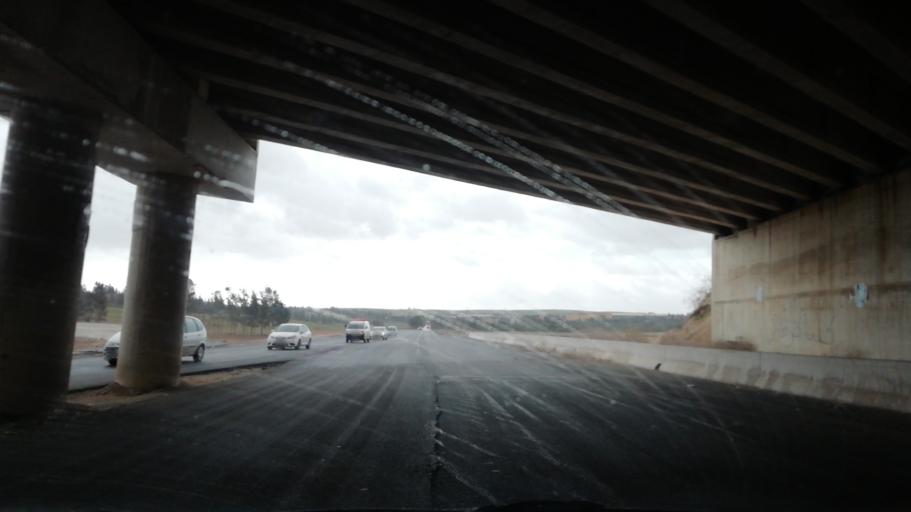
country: DZ
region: Oran
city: Sidi ech Chahmi
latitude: 35.6423
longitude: -0.5259
